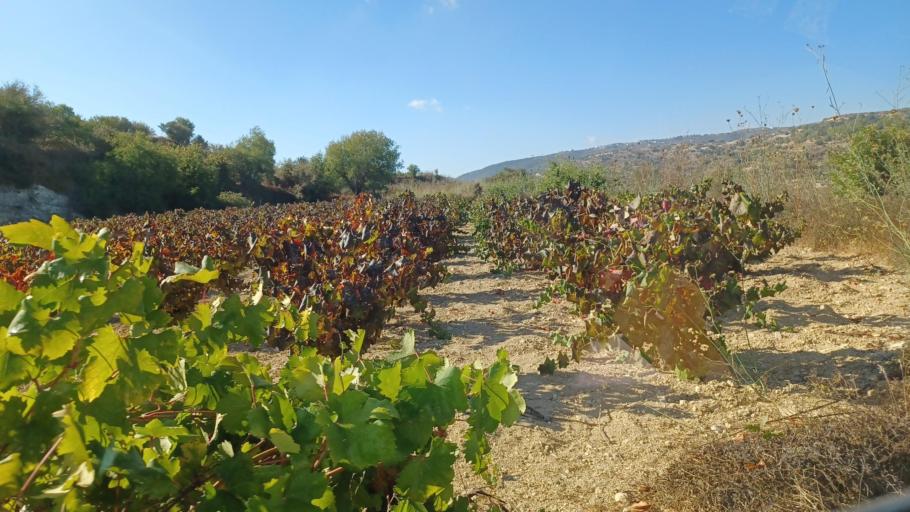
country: CY
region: Pafos
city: Mesogi
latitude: 34.8427
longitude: 32.5213
